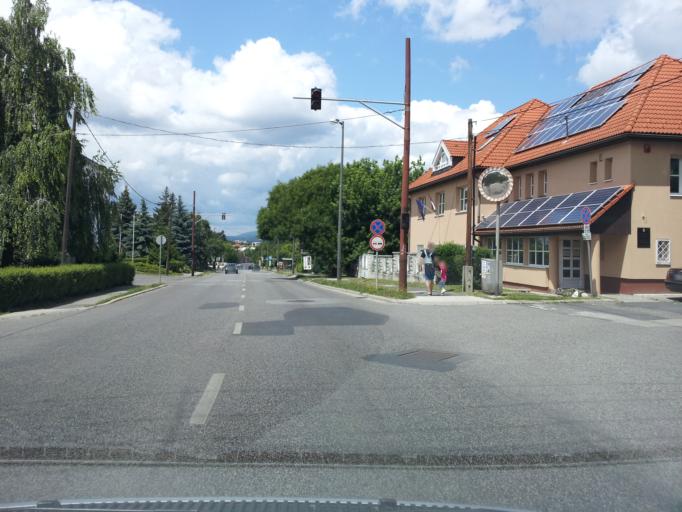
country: HU
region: Veszprem
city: Veszprem
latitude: 47.0938
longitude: 17.9010
